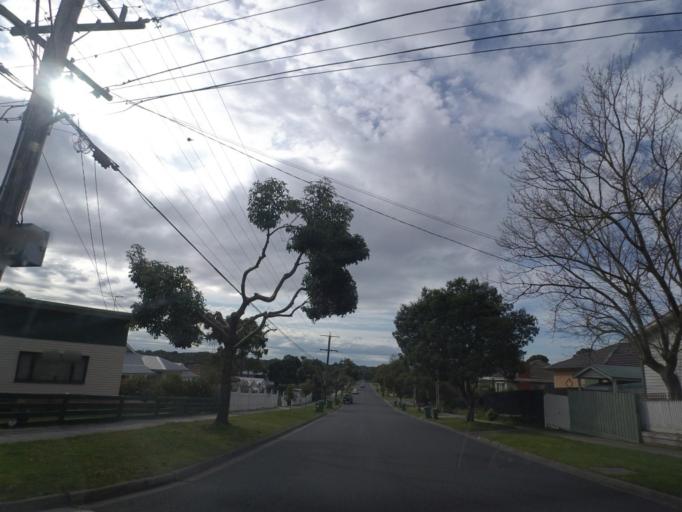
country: AU
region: Victoria
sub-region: Maroondah
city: Heathmont
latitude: -37.8314
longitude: 145.2374
